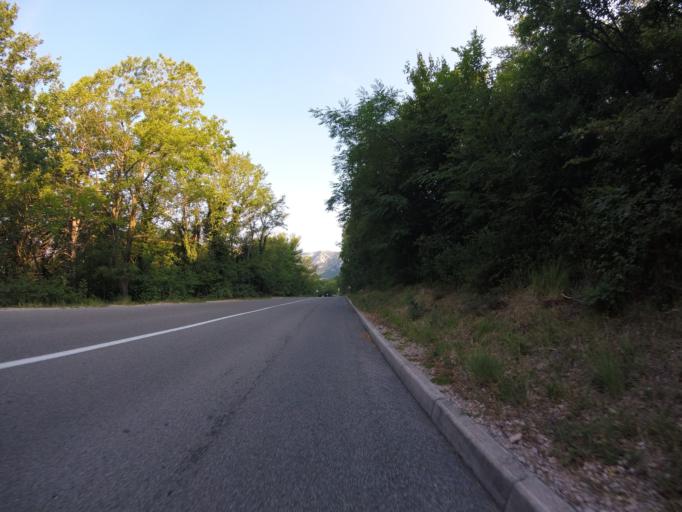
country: HR
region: Primorsko-Goranska
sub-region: Grad Crikvenica
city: Crikvenica
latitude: 45.2099
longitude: 14.7120
